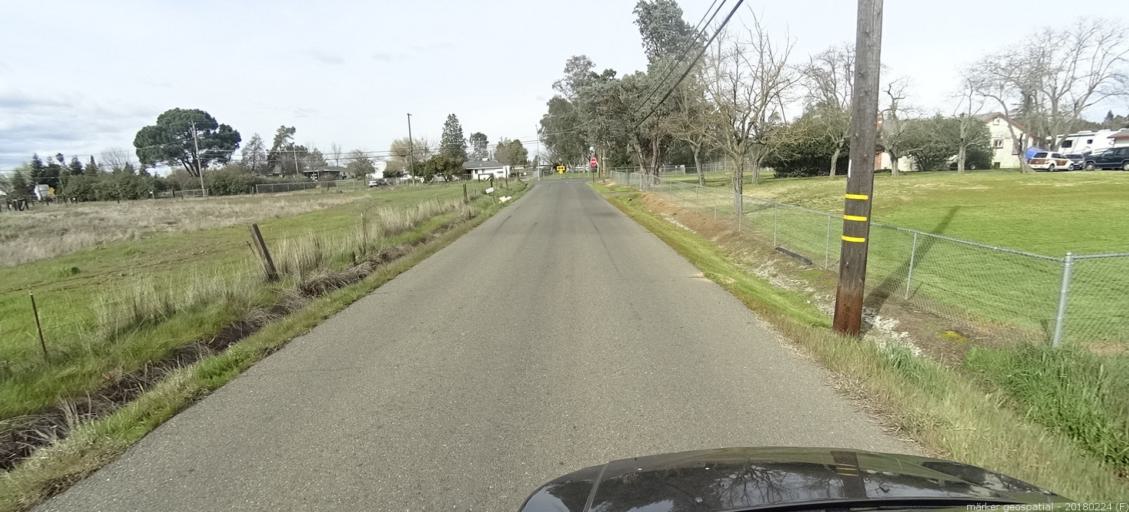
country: US
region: California
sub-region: Sacramento County
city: Rio Linda
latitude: 38.7042
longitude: -121.4476
